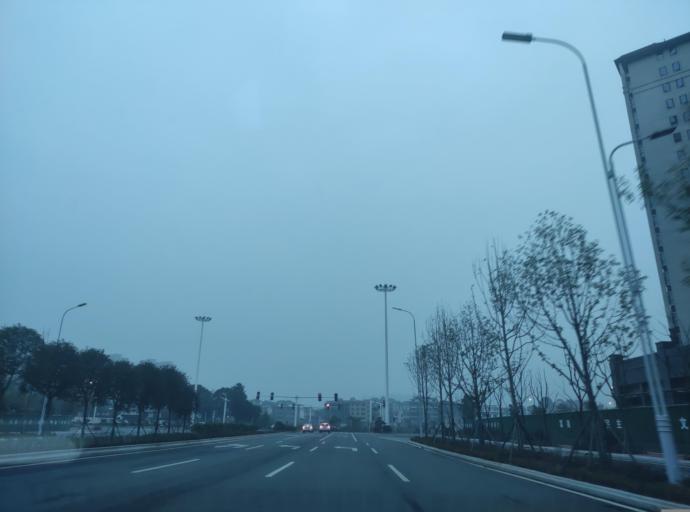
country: CN
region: Jiangxi Sheng
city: Pingxiang
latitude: 27.6637
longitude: 113.8415
